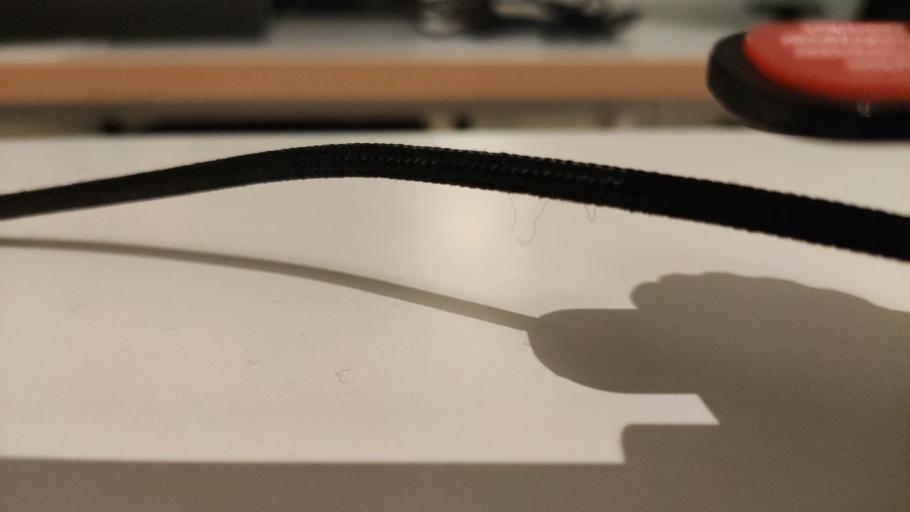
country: RU
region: Moskovskaya
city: Dmitrov
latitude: 56.3528
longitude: 37.5144
